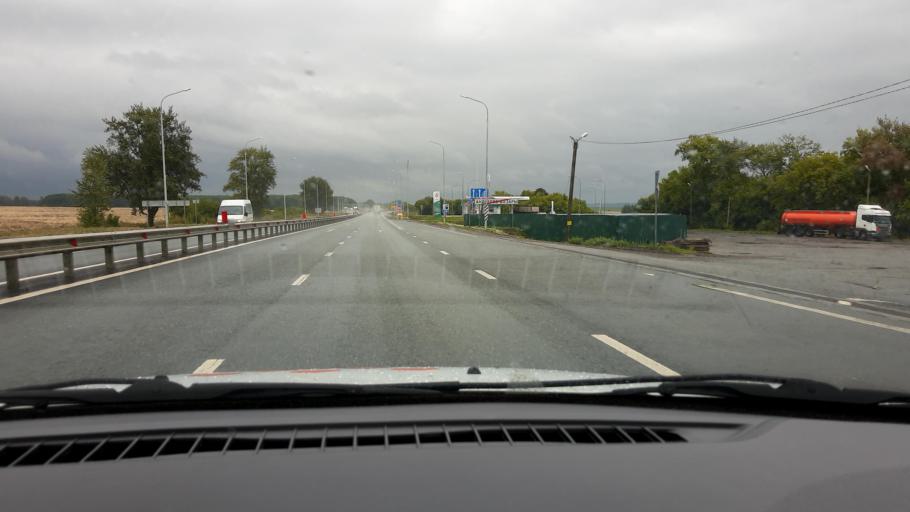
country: RU
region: Chuvashia
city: Yantikovo
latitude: 55.7943
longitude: 47.8185
